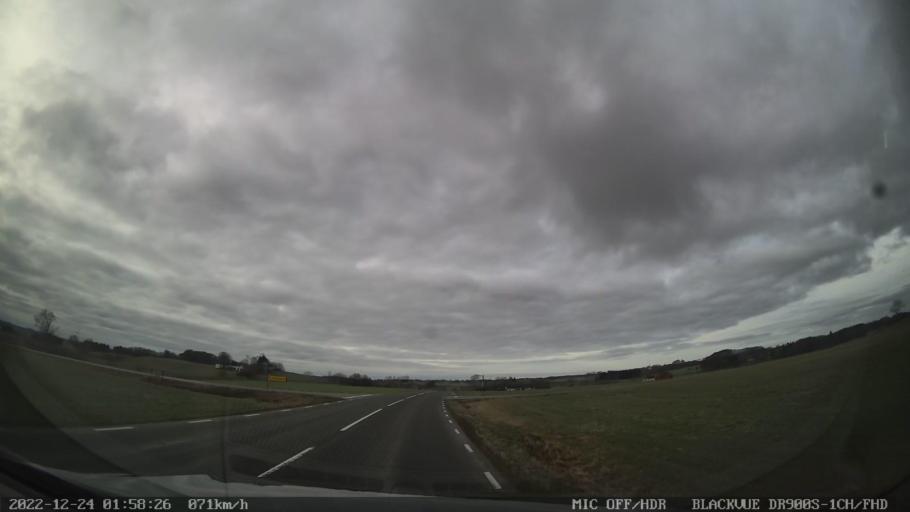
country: SE
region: Skane
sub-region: Tomelilla Kommun
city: Tomelilla
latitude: 55.6036
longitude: 14.0326
